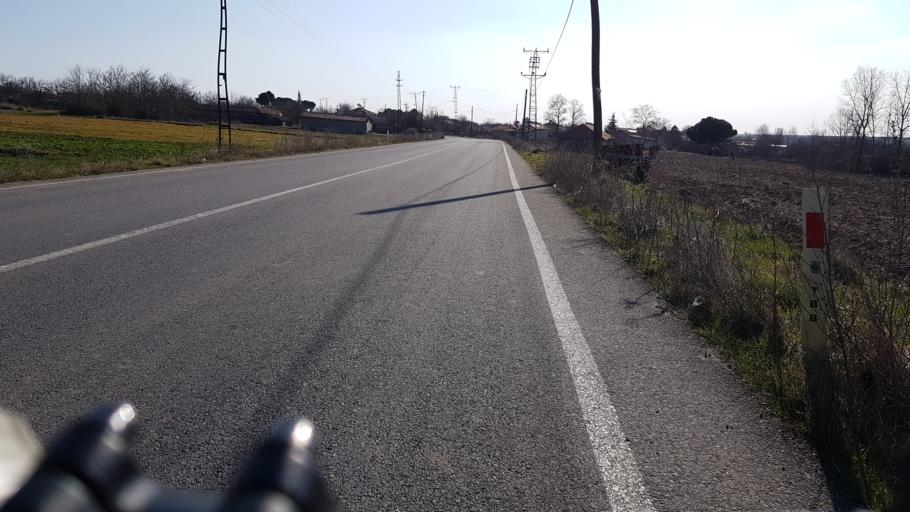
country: TR
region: Tekirdag
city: Velimese
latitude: 41.3480
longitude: 27.8372
